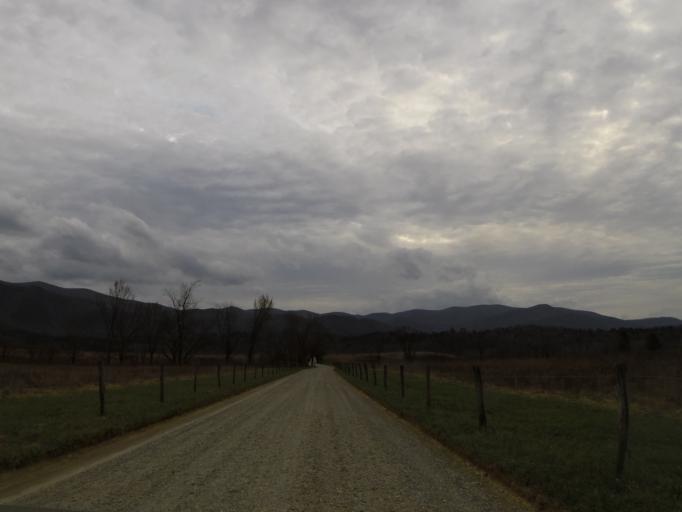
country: US
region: Tennessee
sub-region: Blount County
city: Wildwood
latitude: 35.6002
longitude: -83.8239
